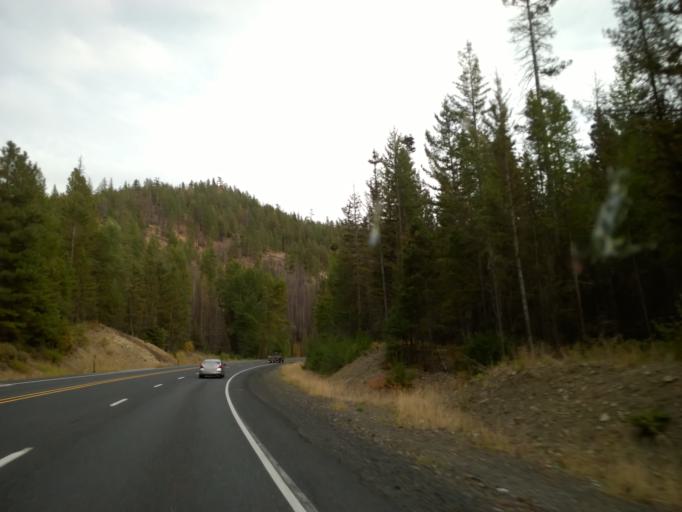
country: US
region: Washington
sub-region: Chelan County
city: Cashmere
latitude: 47.3601
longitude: -120.5641
